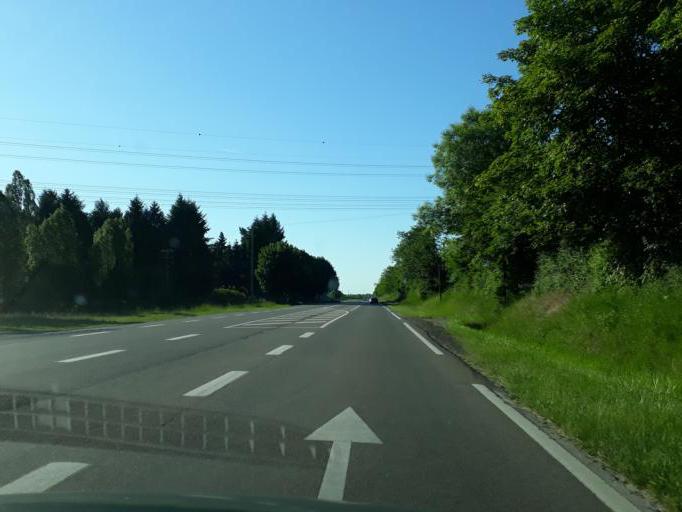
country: FR
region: Bourgogne
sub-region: Departement de la Nievre
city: Neuvy-sur-Loire
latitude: 47.5320
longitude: 2.8660
